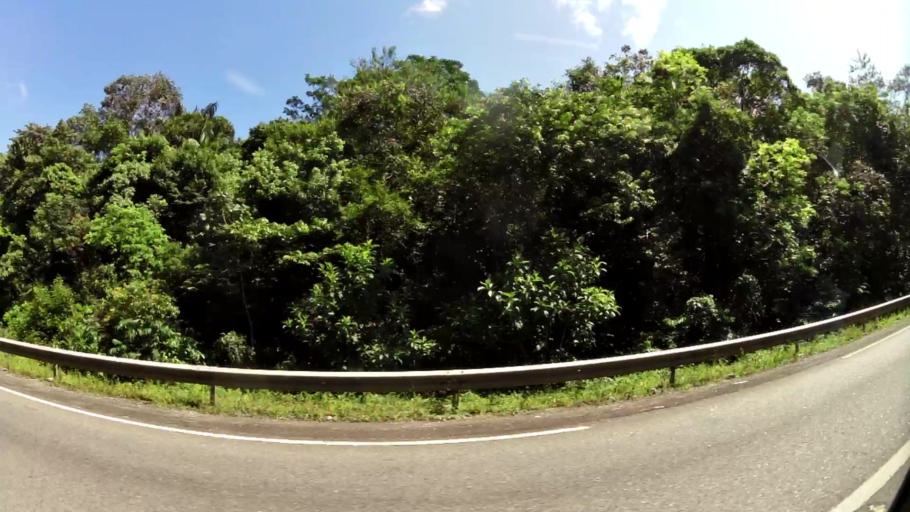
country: GF
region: Guyane
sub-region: Guyane
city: Matoury
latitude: 4.8372
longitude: -52.3406
